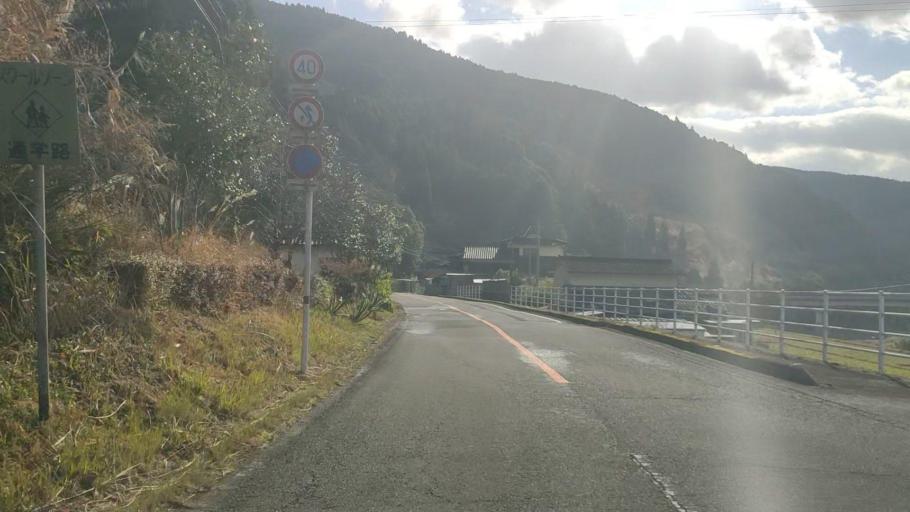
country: JP
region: Kumamoto
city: Hitoyoshi
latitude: 32.3151
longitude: 130.8458
